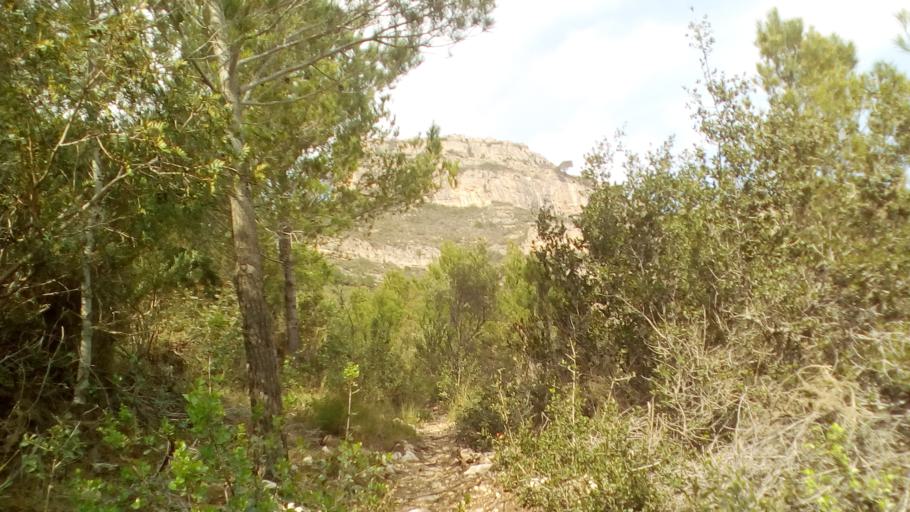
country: ES
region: Valencia
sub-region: Provincia de Valencia
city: Xeraco,Jaraco
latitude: 39.0375
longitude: -0.2358
